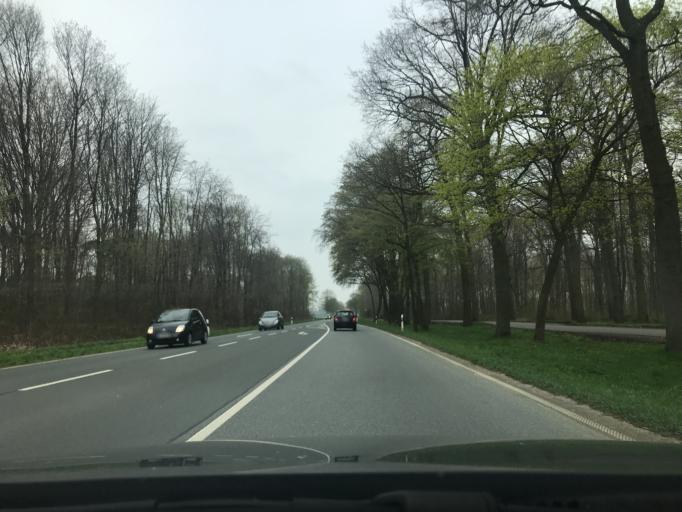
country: DE
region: North Rhine-Westphalia
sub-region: Regierungsbezirk Dusseldorf
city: Kevelaer
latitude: 51.6034
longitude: 6.2289
